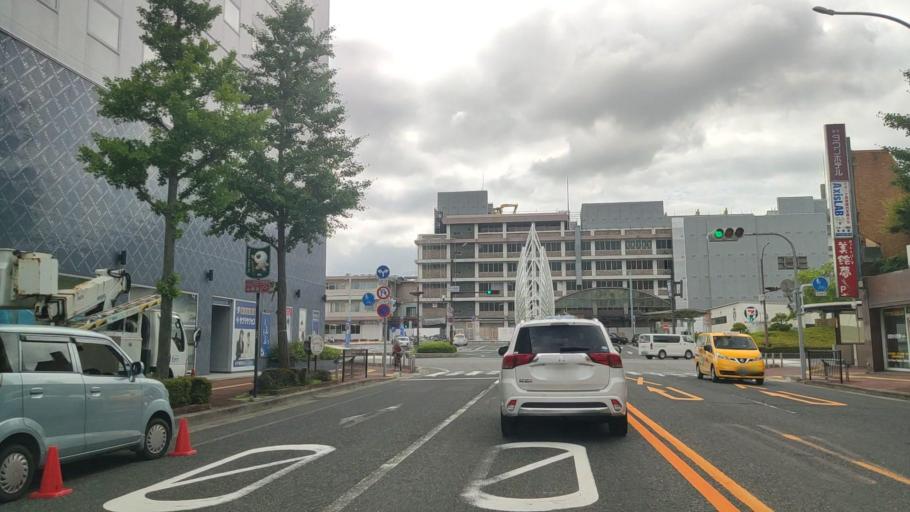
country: JP
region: Tottori
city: Yonago
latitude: 35.4239
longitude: 133.3351
